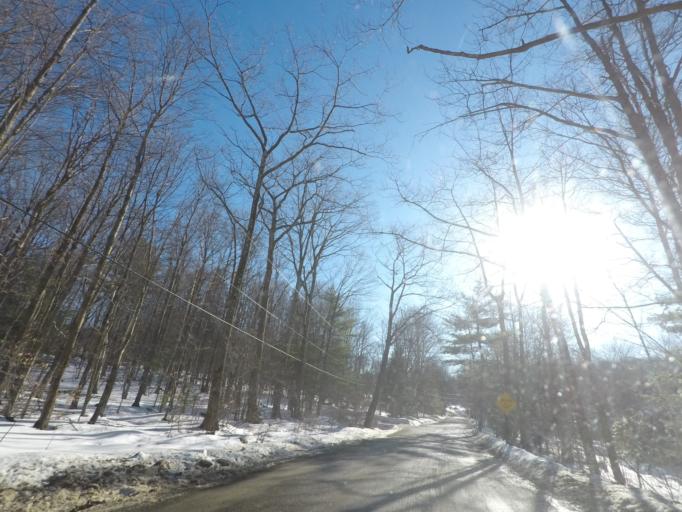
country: US
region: New York
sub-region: Rensselaer County
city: Averill Park
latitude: 42.6435
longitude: -73.5022
